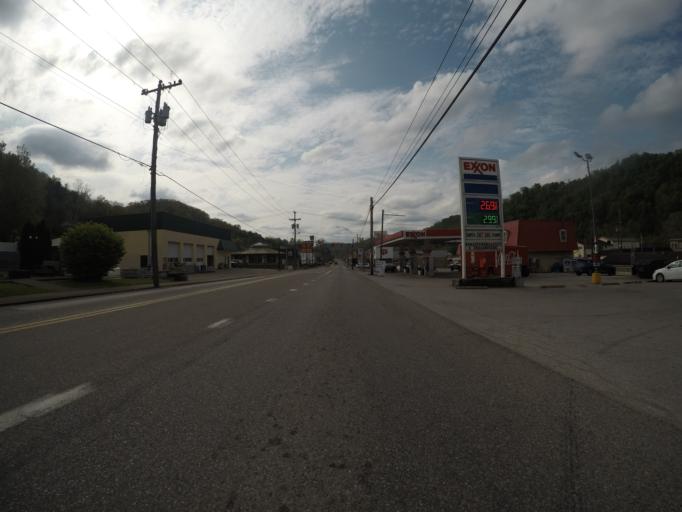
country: US
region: West Virginia
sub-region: Boone County
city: Madison
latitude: 38.0814
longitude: -81.8345
